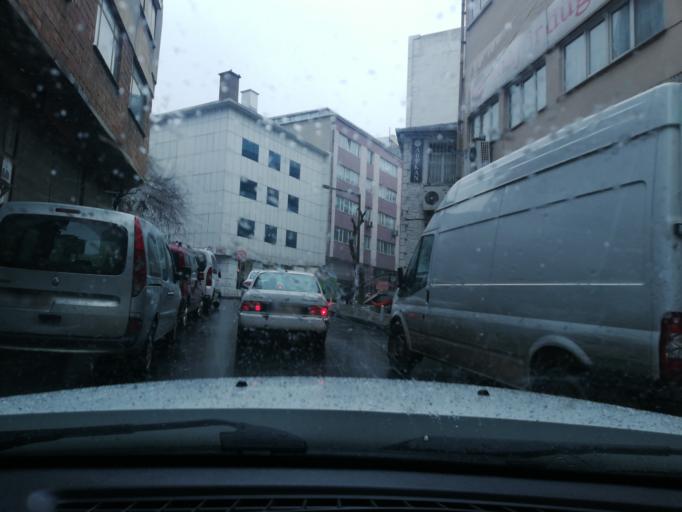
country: TR
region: Istanbul
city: Sisli
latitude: 41.0727
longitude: 28.9813
